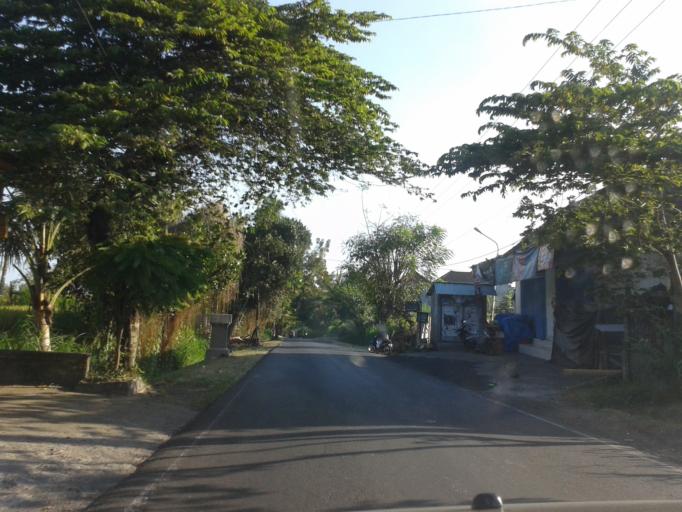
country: ID
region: Bali
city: Banjar Wangsian
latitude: -8.5079
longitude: 115.4026
